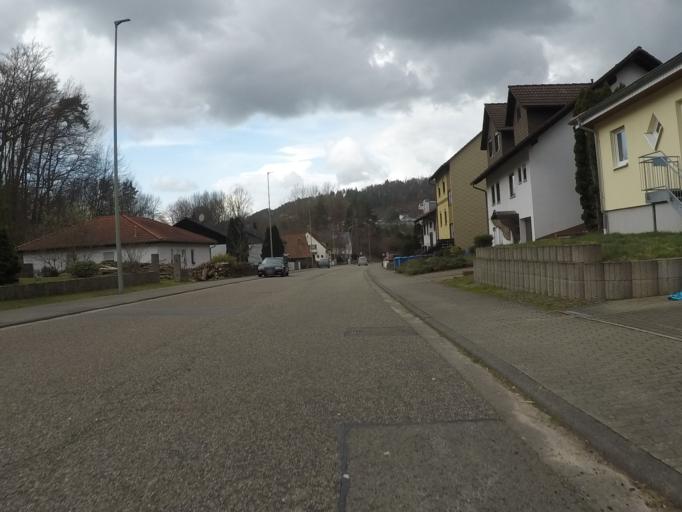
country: DE
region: Rheinland-Pfalz
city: Rodalben
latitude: 49.2335
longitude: 7.6572
